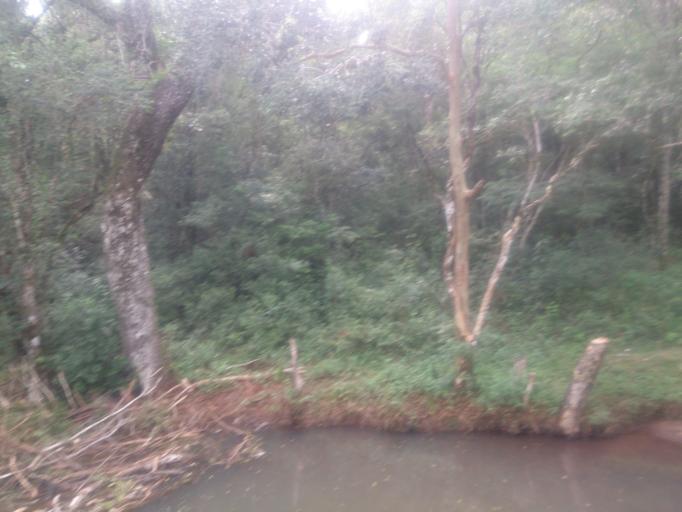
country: AR
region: Misiones
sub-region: Departamento de Obera
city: Obera
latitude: -27.4460
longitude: -55.1122
